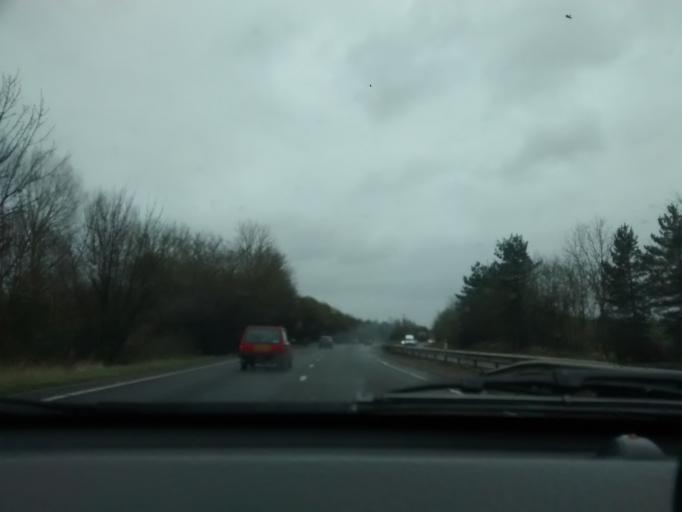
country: GB
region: England
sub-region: Suffolk
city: Needham Market
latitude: 52.1785
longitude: 1.0457
